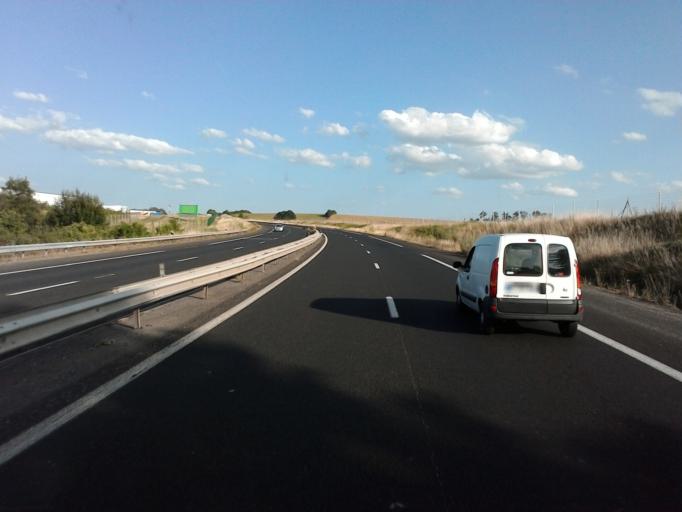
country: FR
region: Lorraine
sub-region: Departement de Meurthe-et-Moselle
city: Flavigny-sur-Moselle
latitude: 48.5626
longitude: 6.1772
